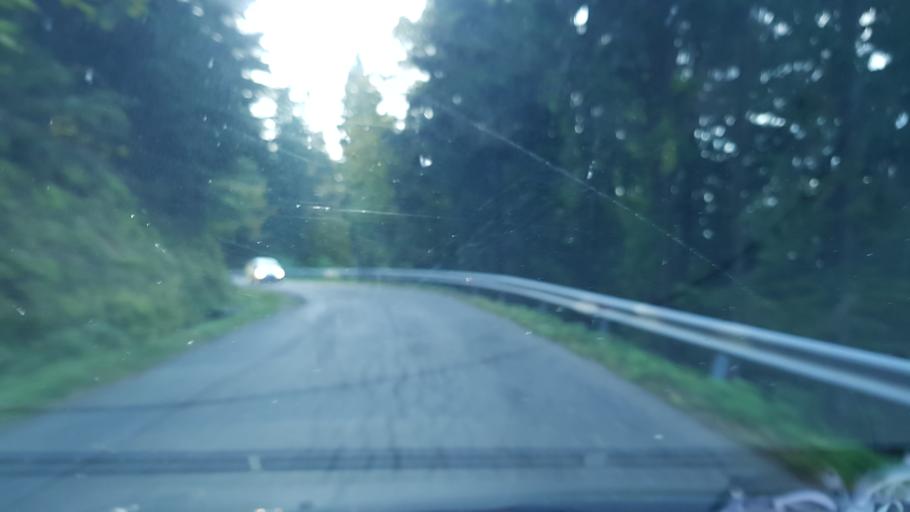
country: SI
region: Slovenj Gradec
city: Legen
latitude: 46.4862
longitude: 15.1565
